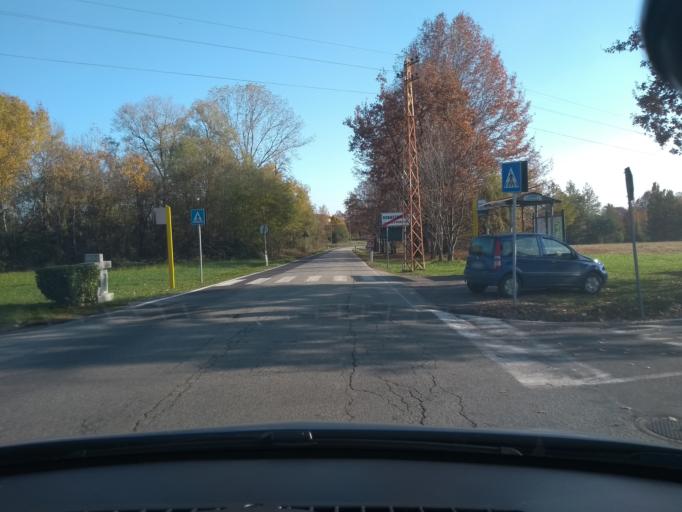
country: IT
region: Piedmont
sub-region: Provincia di Torino
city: Robassomero
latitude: 45.2074
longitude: 7.5523
